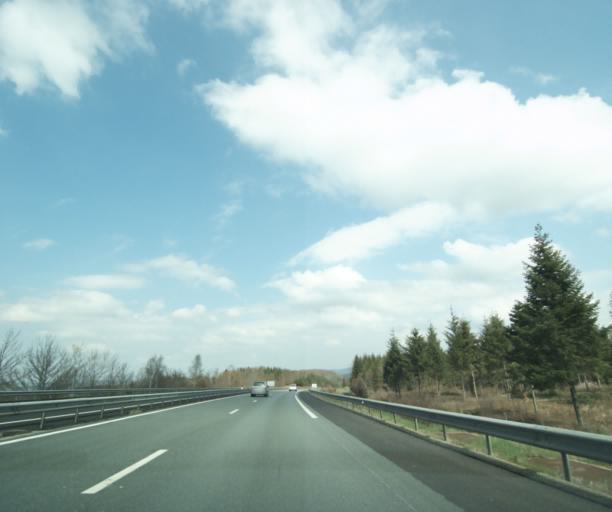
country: FR
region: Auvergne
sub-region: Departement du Cantal
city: Massiac
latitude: 45.1592
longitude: 3.1476
